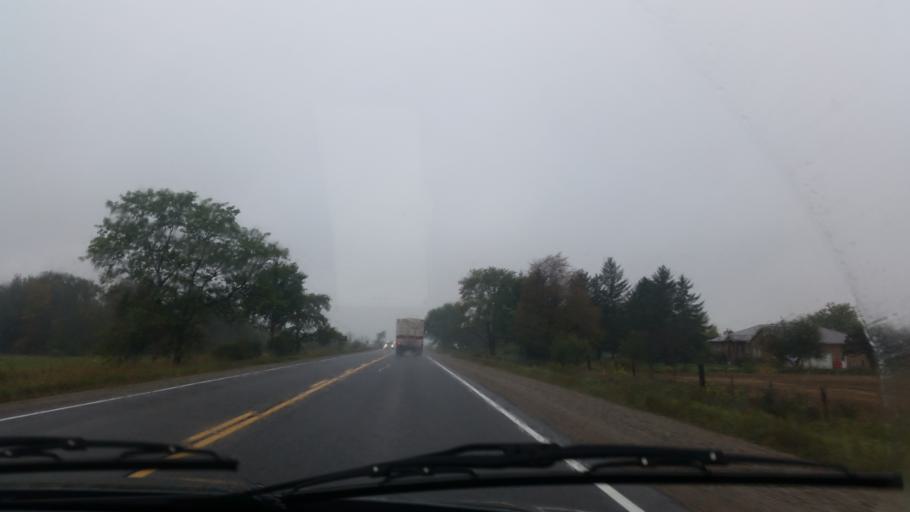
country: CA
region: Ontario
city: London
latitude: 43.1727
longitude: -81.3340
